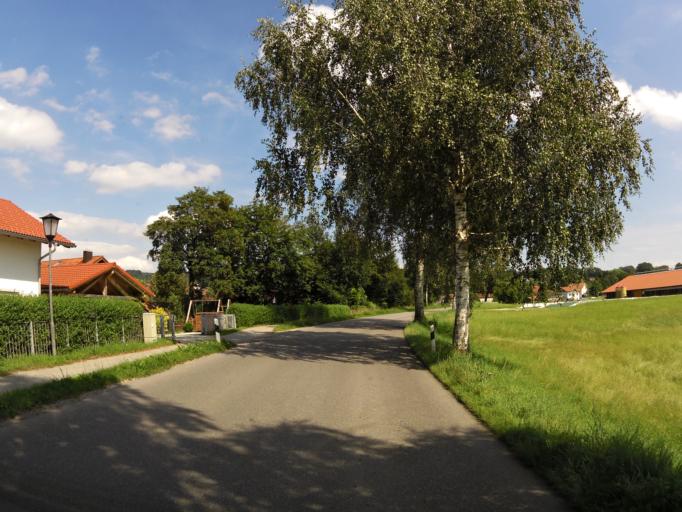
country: DE
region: Bavaria
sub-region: Upper Bavaria
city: Pahl
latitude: 47.9277
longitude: 11.1517
